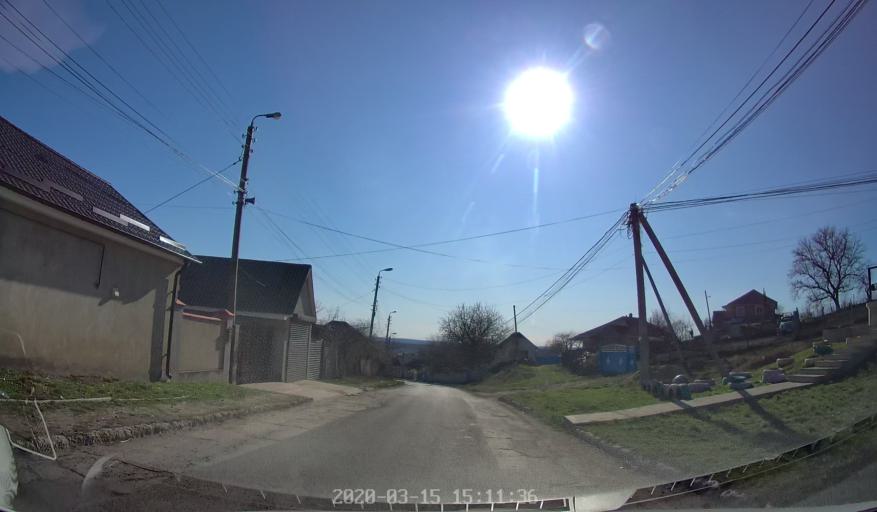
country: MD
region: Orhei
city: Orhei
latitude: 47.2618
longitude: 28.7763
